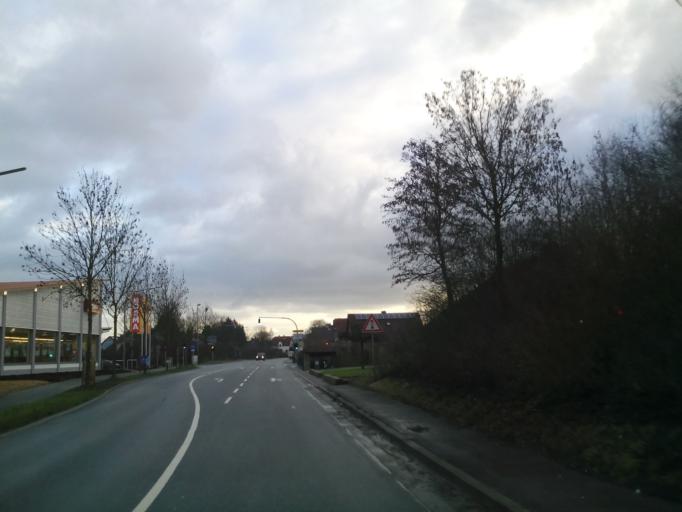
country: DE
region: Bavaria
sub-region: Upper Franconia
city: Michelau
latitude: 50.1642
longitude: 11.0996
